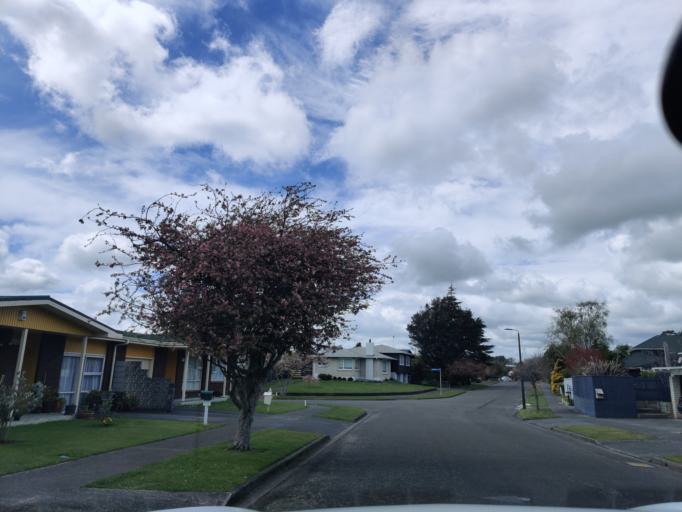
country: NZ
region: Manawatu-Wanganui
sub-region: Palmerston North City
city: Palmerston North
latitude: -40.3809
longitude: 175.5931
